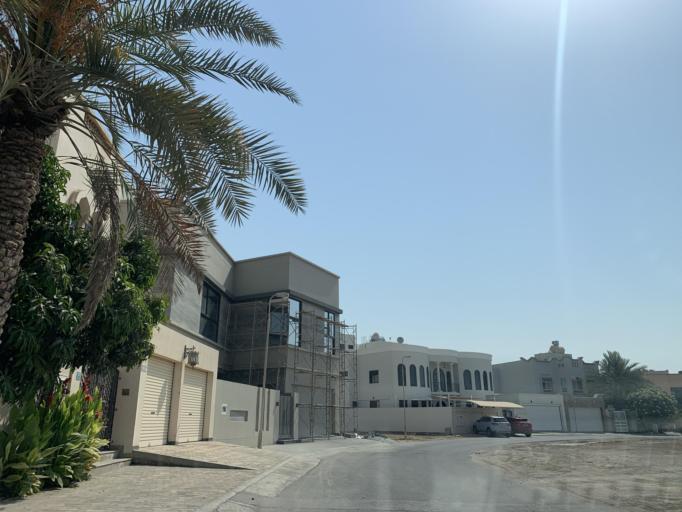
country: BH
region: Northern
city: Madinat `Isa
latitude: 26.1924
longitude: 50.5092
